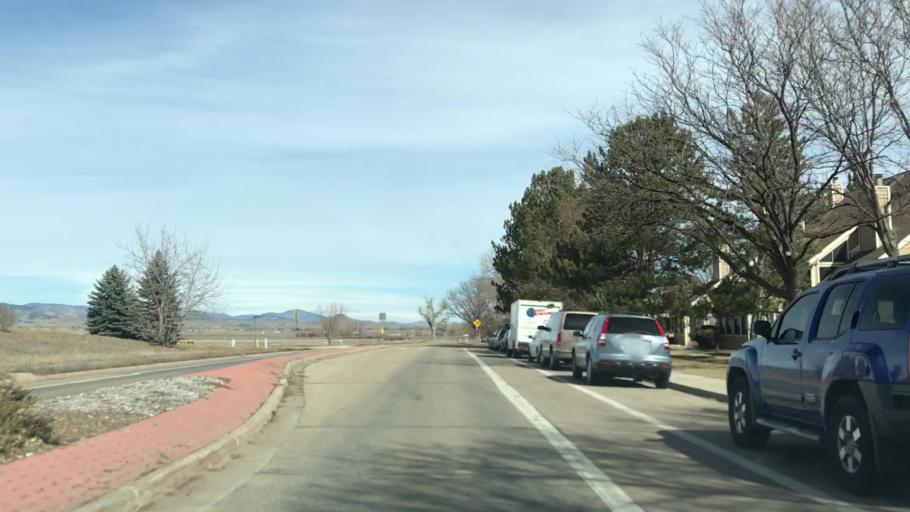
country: US
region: Colorado
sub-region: Boulder County
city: Gunbarrel
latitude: 40.0610
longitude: -105.2161
